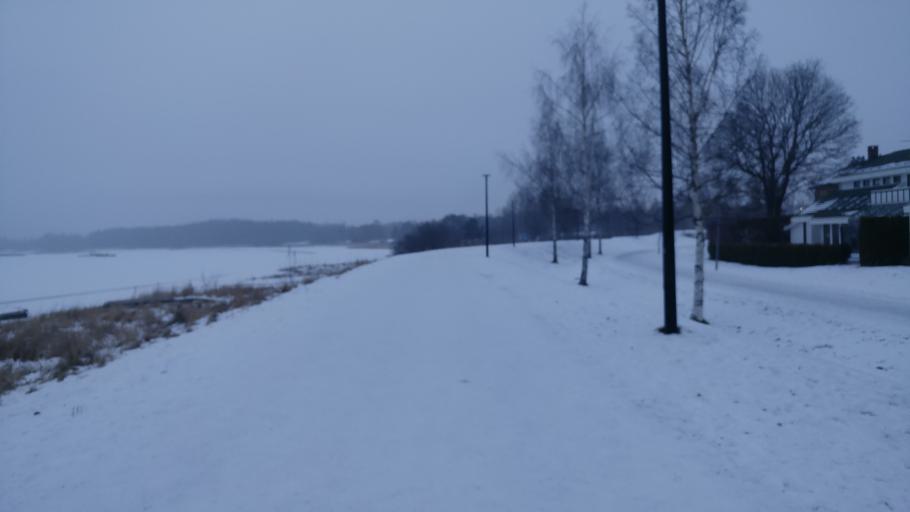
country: NO
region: Akershus
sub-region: Skedsmo
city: Lillestrom
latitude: 59.9614
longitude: 11.0290
